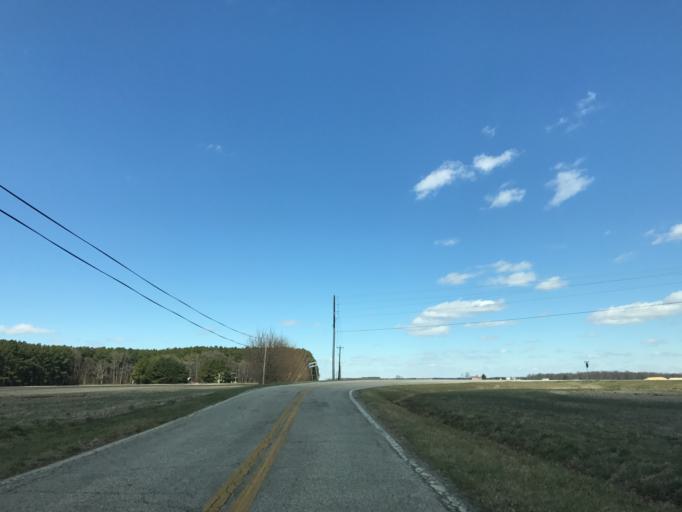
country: US
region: Maryland
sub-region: Caroline County
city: Greensboro
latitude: 39.1006
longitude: -75.8748
